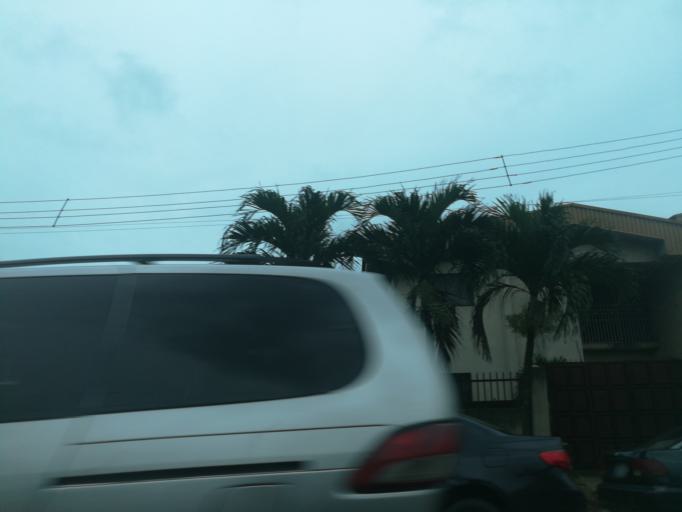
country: NG
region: Rivers
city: Port Harcourt
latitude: 4.8131
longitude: 7.0019
